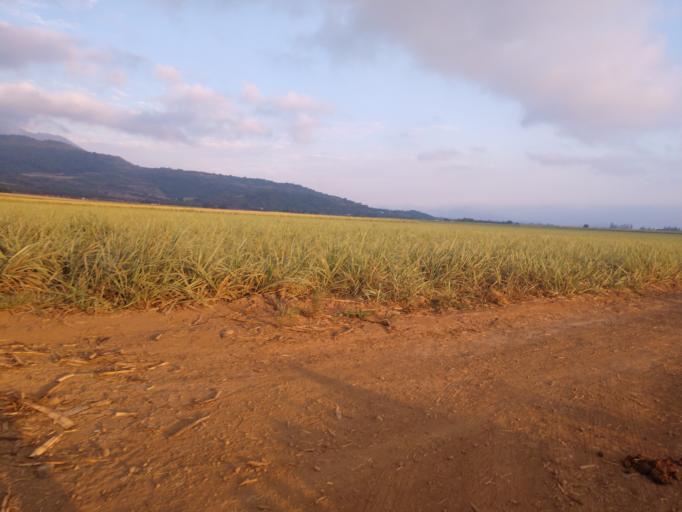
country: MX
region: Nayarit
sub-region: Tepic
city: La Corregidora
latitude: 21.4834
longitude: -104.8047
